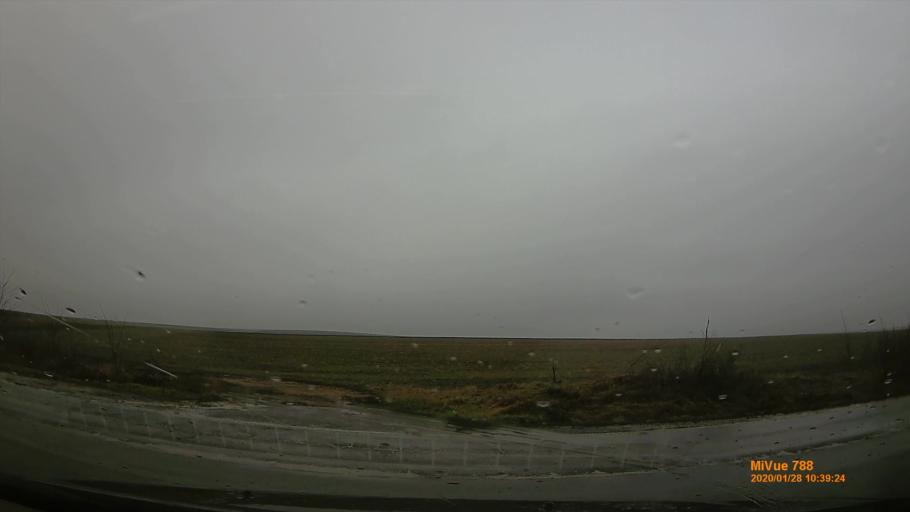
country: HU
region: Pest
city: Gomba
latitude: 47.3611
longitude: 19.4898
